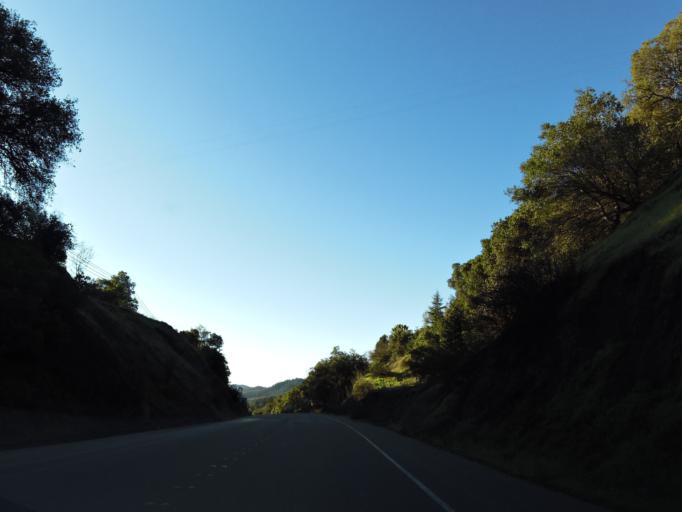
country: US
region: California
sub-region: Sonoma County
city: Cloverdale
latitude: 38.8171
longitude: -123.0233
